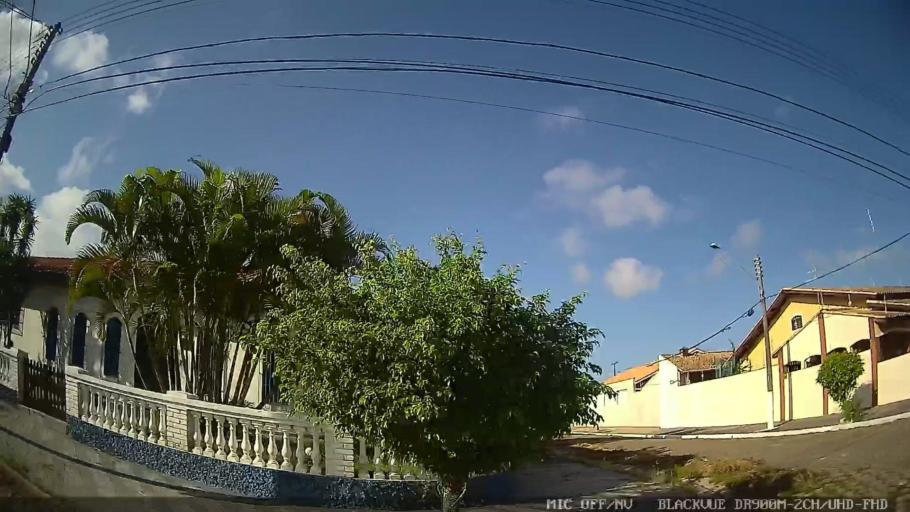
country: BR
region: Sao Paulo
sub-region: Peruibe
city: Peruibe
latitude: -24.2907
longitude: -46.9669
